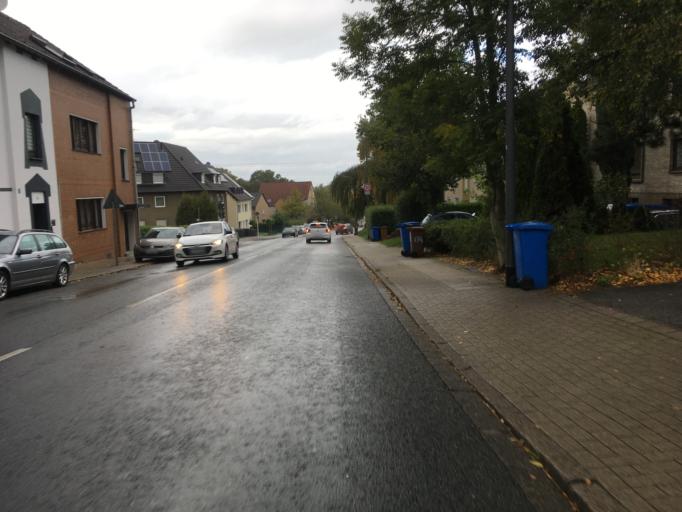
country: DE
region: North Rhine-Westphalia
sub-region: Regierungsbezirk Munster
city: Bottrop
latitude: 51.4841
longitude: 6.9324
